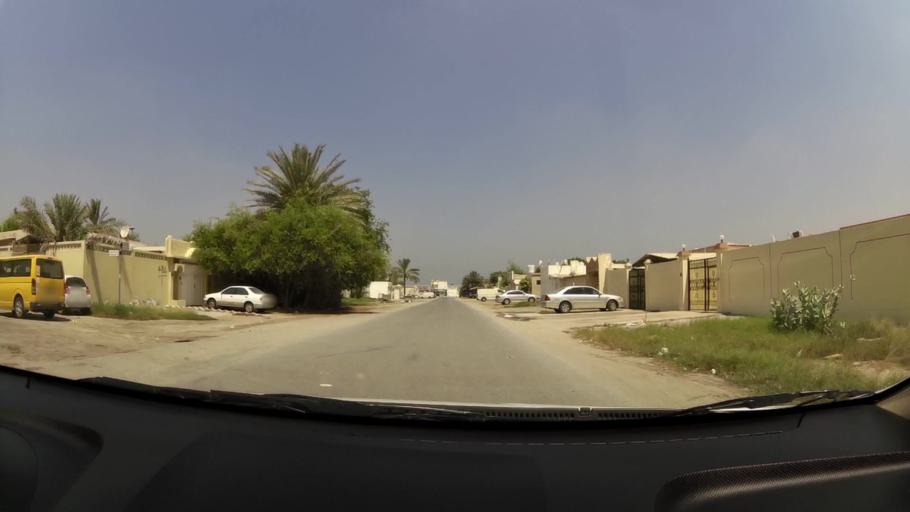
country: AE
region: Umm al Qaywayn
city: Umm al Qaywayn
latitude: 25.5604
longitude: 55.5568
